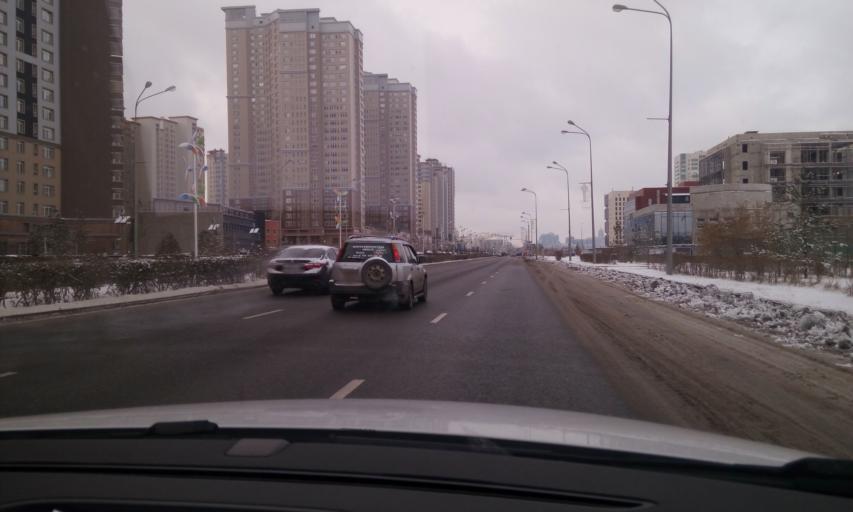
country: KZ
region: Astana Qalasy
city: Astana
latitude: 51.1281
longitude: 71.4677
